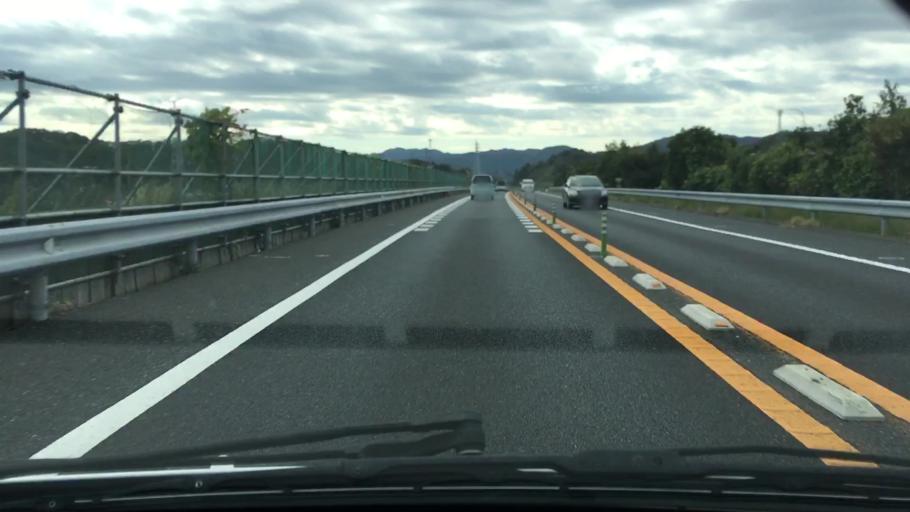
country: JP
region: Chiba
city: Kimitsu
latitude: 35.2367
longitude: 139.8881
